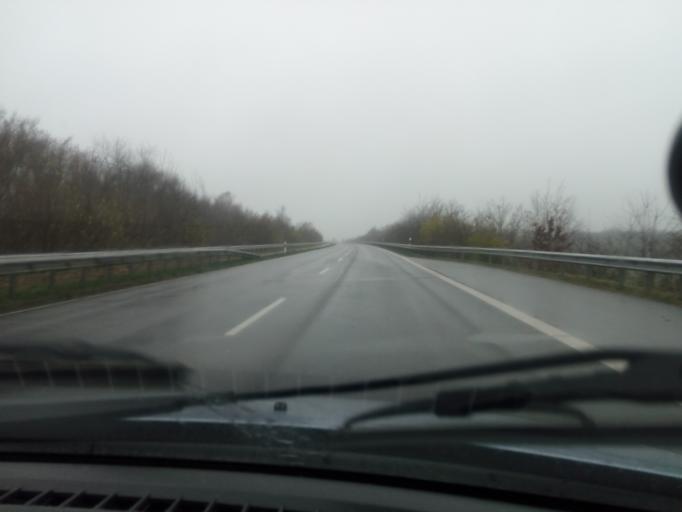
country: DE
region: Lower Saxony
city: Lehe
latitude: 52.9907
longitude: 7.3572
